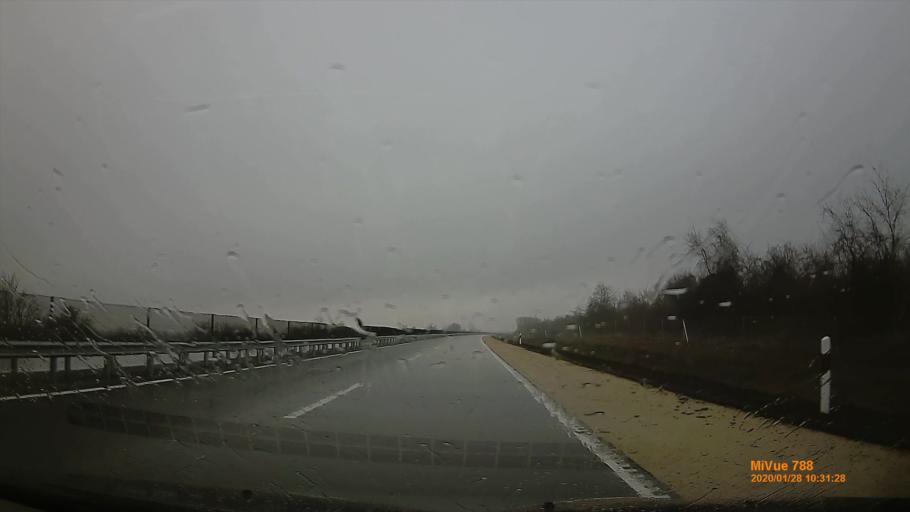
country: HU
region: Pest
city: Gomba
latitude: 47.3393
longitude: 19.5039
